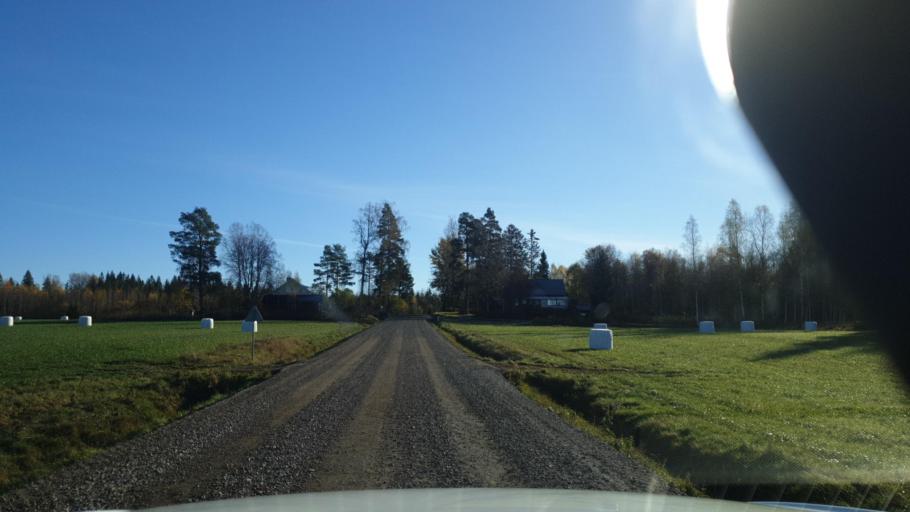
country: SE
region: Vaermland
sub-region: Karlstads Kommun
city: Valberg
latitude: 59.4193
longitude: 13.1130
